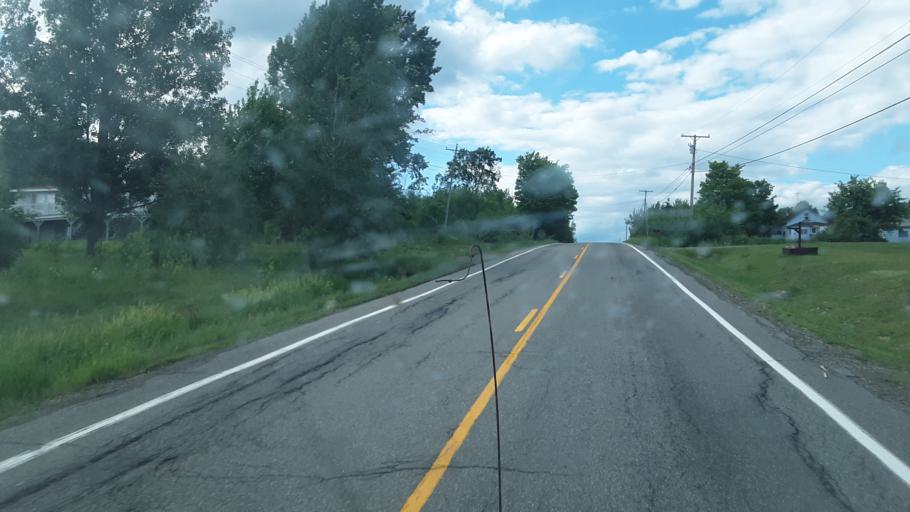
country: US
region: Maine
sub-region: Penobscot County
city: Patten
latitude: 46.0260
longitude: -68.4451
